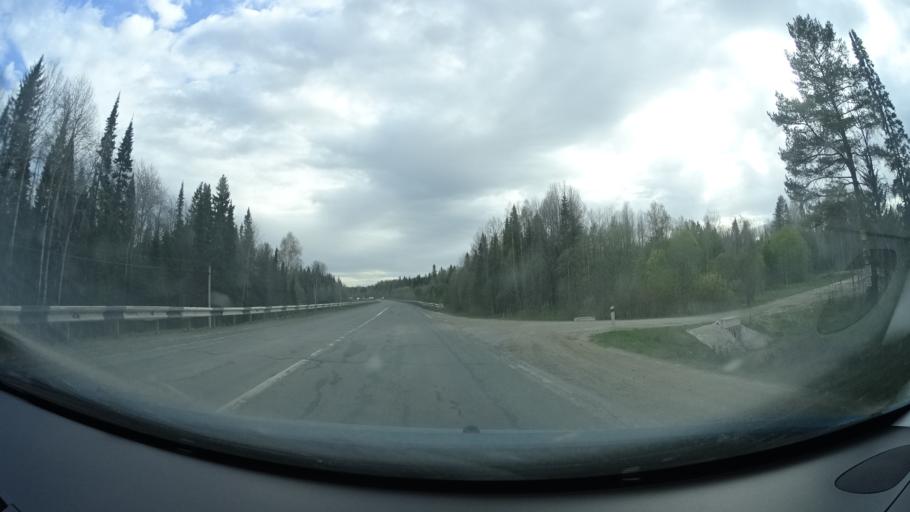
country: RU
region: Perm
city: Kultayevo
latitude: 57.8098
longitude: 55.7889
